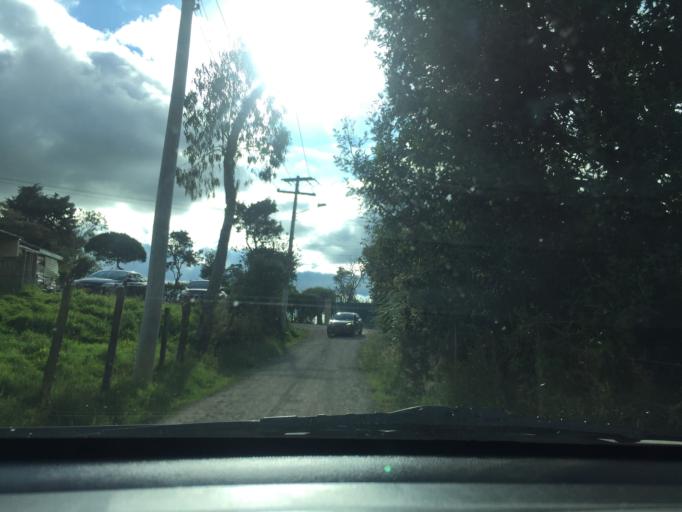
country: CO
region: Cundinamarca
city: Sopo
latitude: 4.9163
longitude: -73.9183
